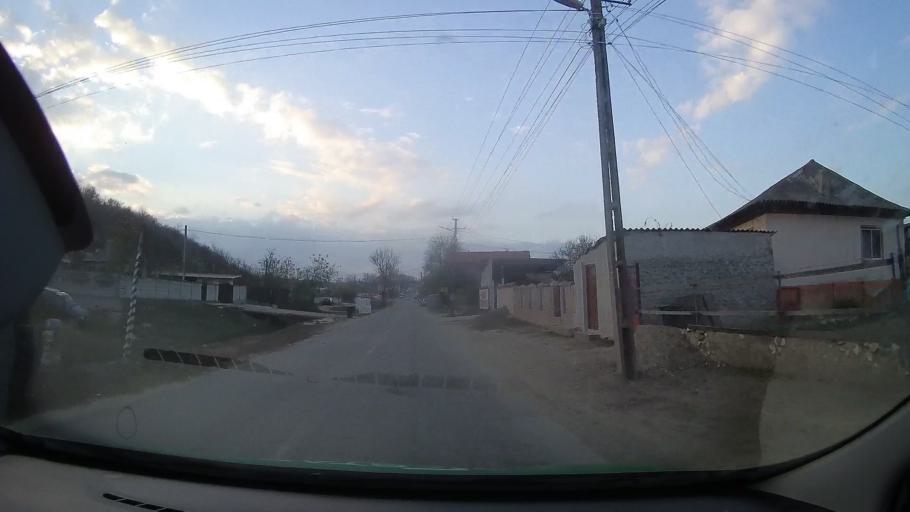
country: RO
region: Constanta
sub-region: Comuna Baneasa
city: Baneasa
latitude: 44.0620
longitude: 27.7050
